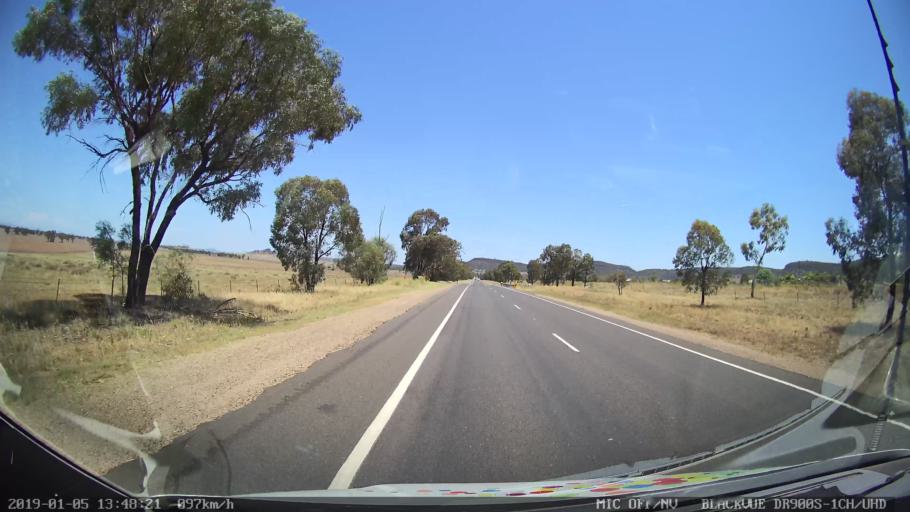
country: AU
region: New South Wales
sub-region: Gunnedah
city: Gunnedah
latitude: -31.0005
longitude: 150.2786
